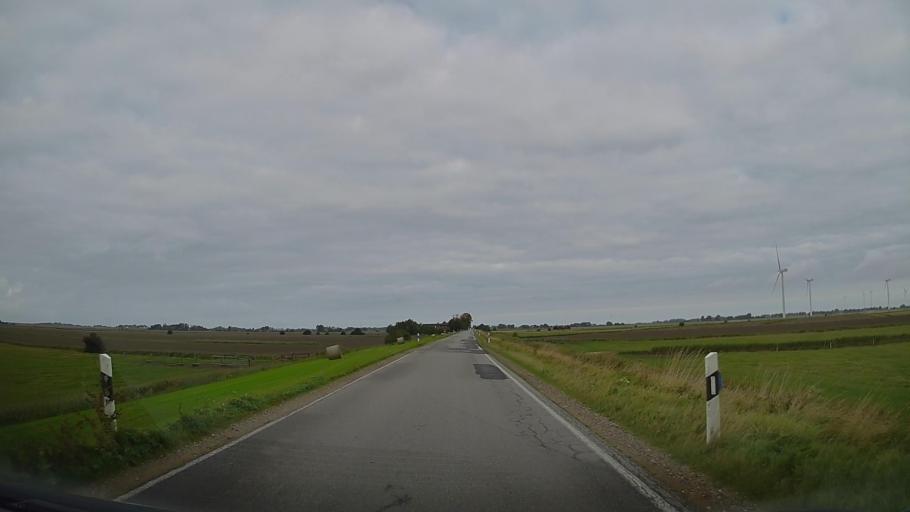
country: DE
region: Schleswig-Holstein
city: Galmsbull
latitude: 54.7872
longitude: 8.7310
